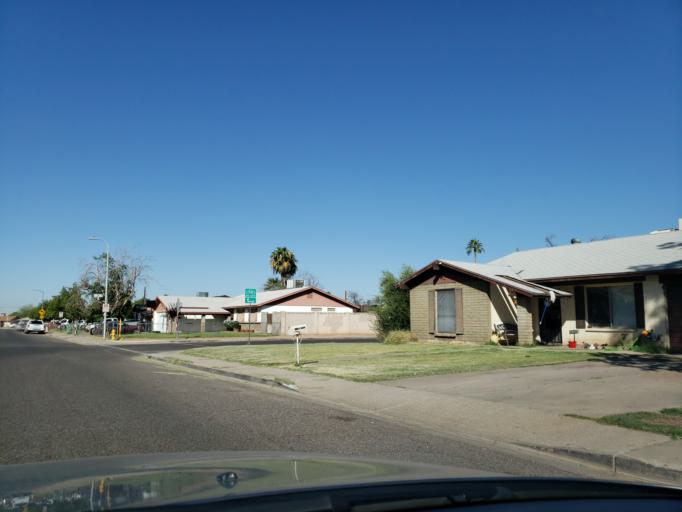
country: US
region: Arizona
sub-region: Maricopa County
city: Glendale
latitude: 33.5007
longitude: -112.2273
